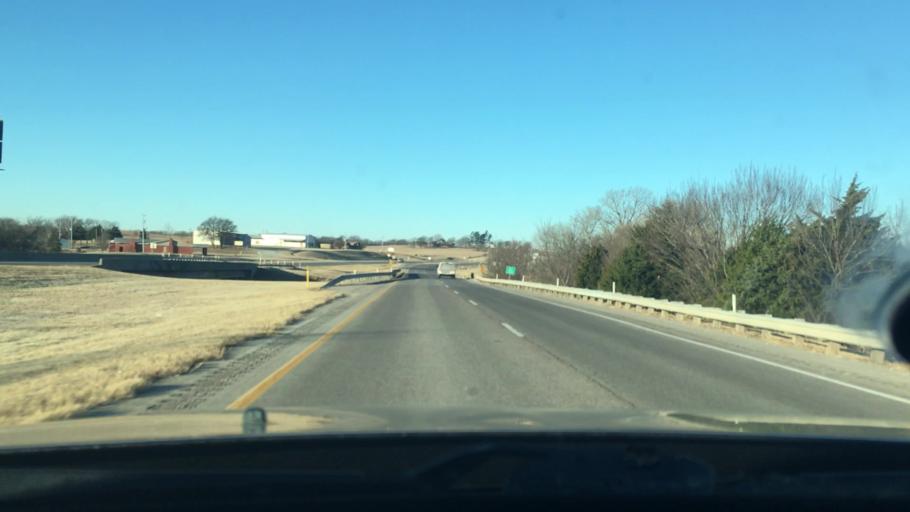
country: US
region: Oklahoma
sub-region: Murray County
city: Sulphur
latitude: 34.5070
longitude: -97.0327
